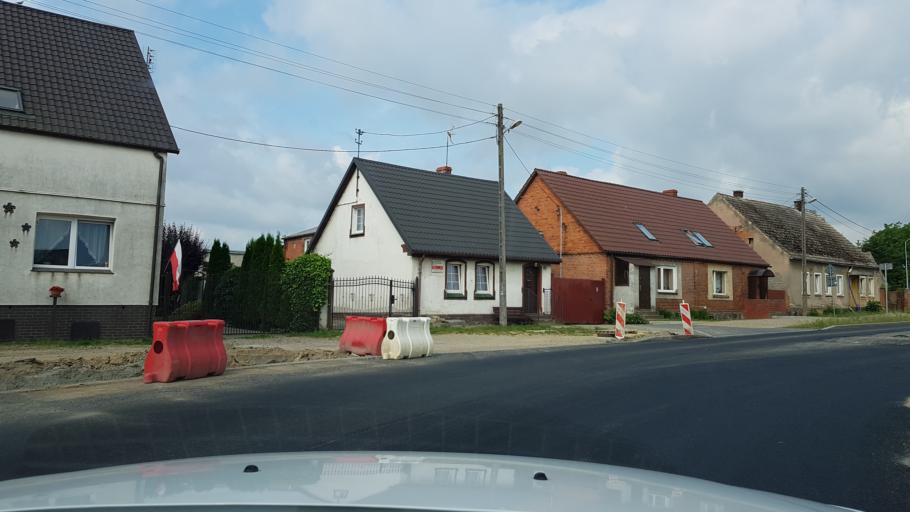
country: PL
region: West Pomeranian Voivodeship
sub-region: Powiat gryfinski
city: Gryfino
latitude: 53.2584
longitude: 14.5735
